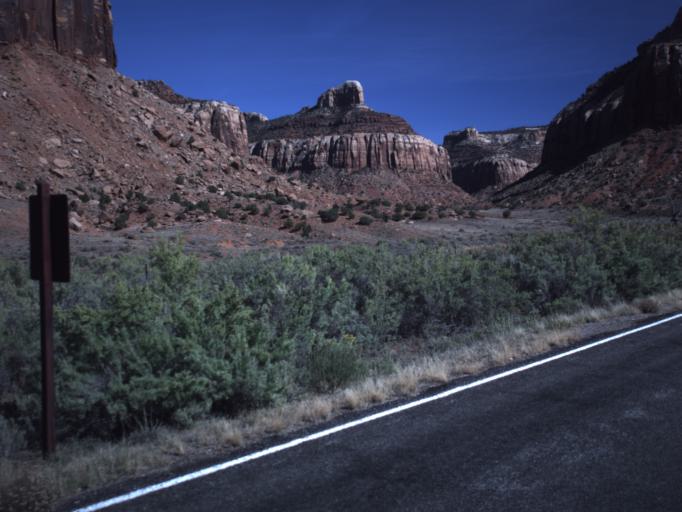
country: US
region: Utah
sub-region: San Juan County
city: Monticello
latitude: 38.0695
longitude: -109.5565
